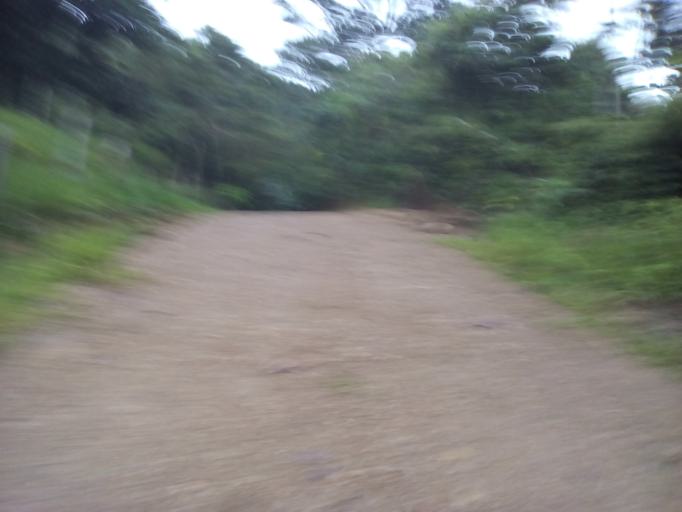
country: CO
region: Casanare
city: Nunchia
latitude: 5.6512
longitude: -72.2918
